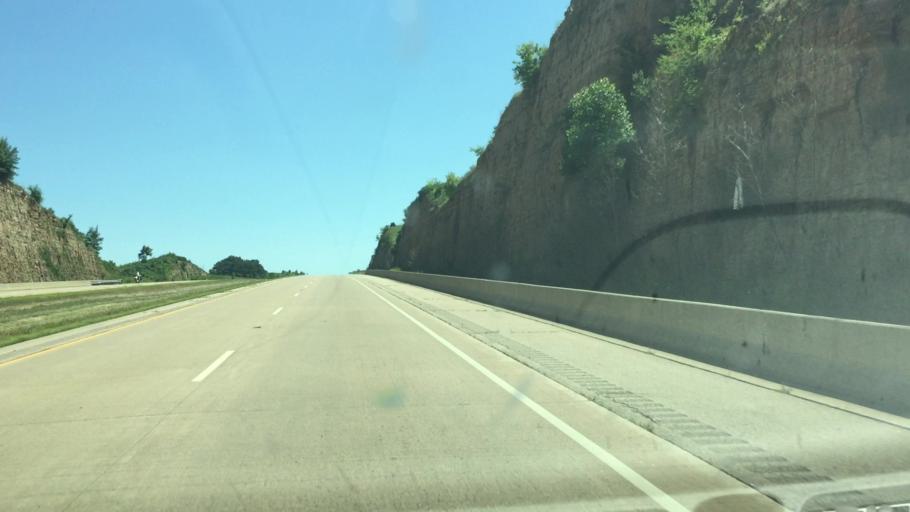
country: US
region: Wisconsin
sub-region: Grant County
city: Dickeyville
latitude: 42.6376
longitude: -90.5789
